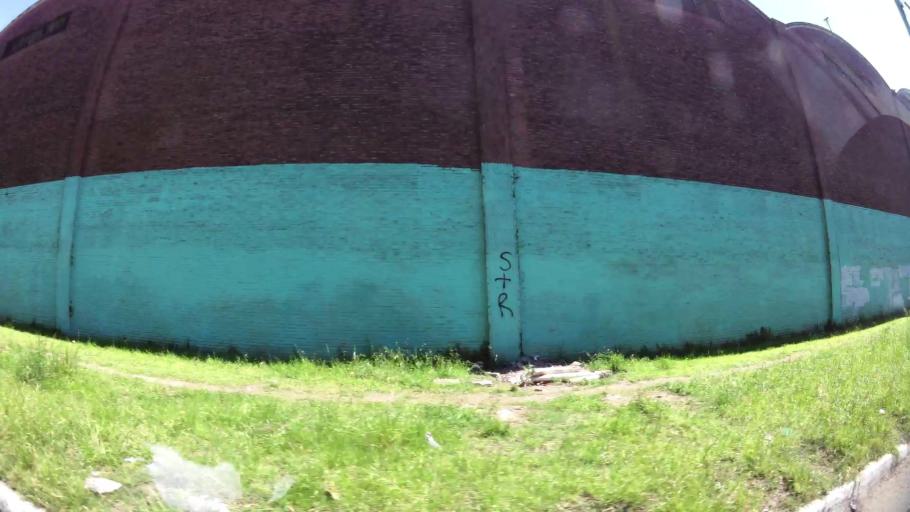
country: AR
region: Buenos Aires
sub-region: Partido de Quilmes
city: Quilmes
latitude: -34.7249
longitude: -58.2824
